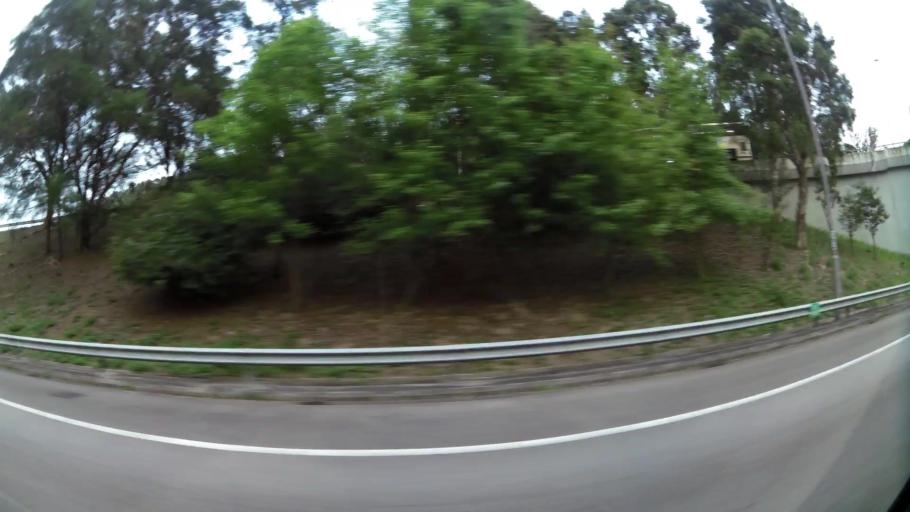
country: HK
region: Sha Tin
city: Sha Tin
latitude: 22.3951
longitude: 114.2100
